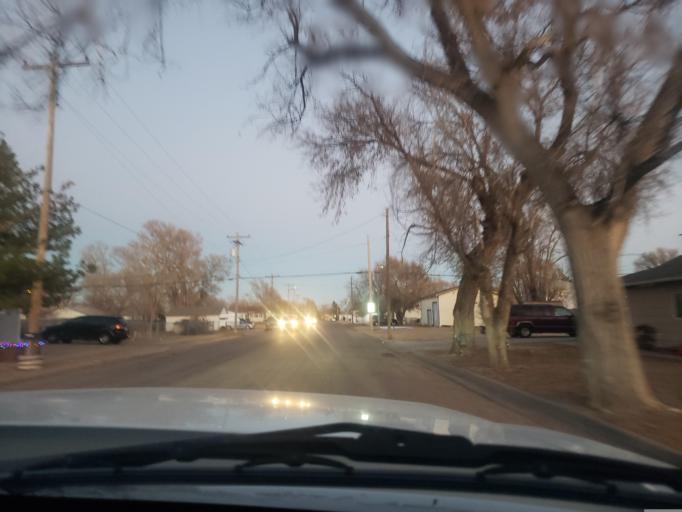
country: US
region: Kansas
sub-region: Finney County
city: Garden City
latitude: 37.9840
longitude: -100.8734
